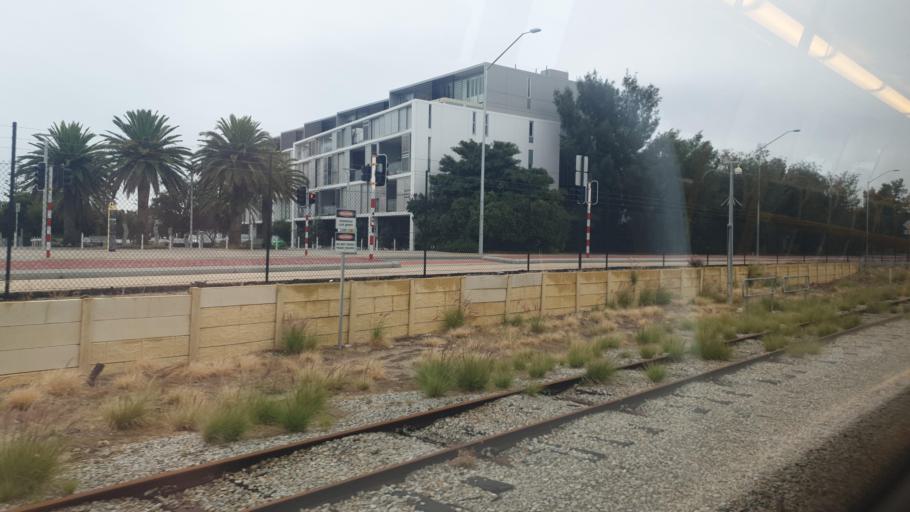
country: AU
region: Western Australia
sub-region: Fremantle
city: North Fremantle
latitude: -32.0296
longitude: 115.7518
